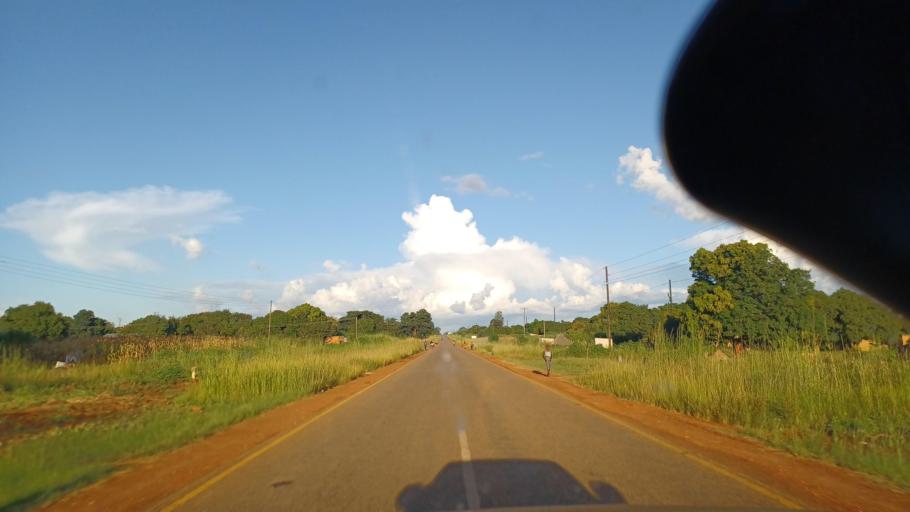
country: ZM
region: North-Western
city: Kalengwa
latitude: -13.1428
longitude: 25.0321
